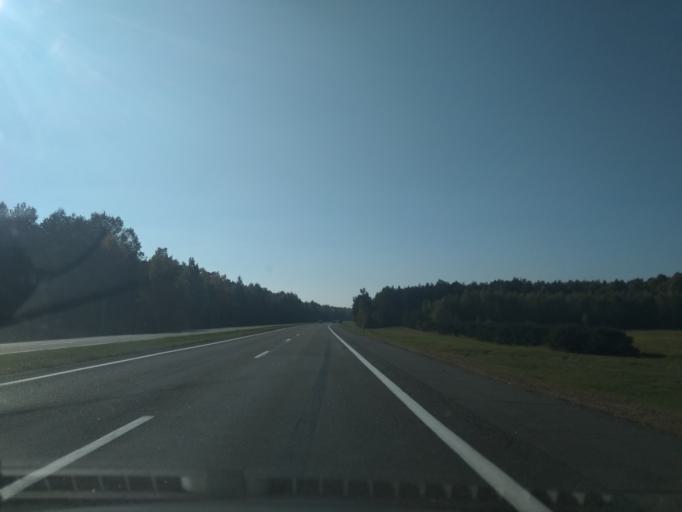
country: BY
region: Brest
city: Ivatsevichy
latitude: 52.7745
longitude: 25.5436
